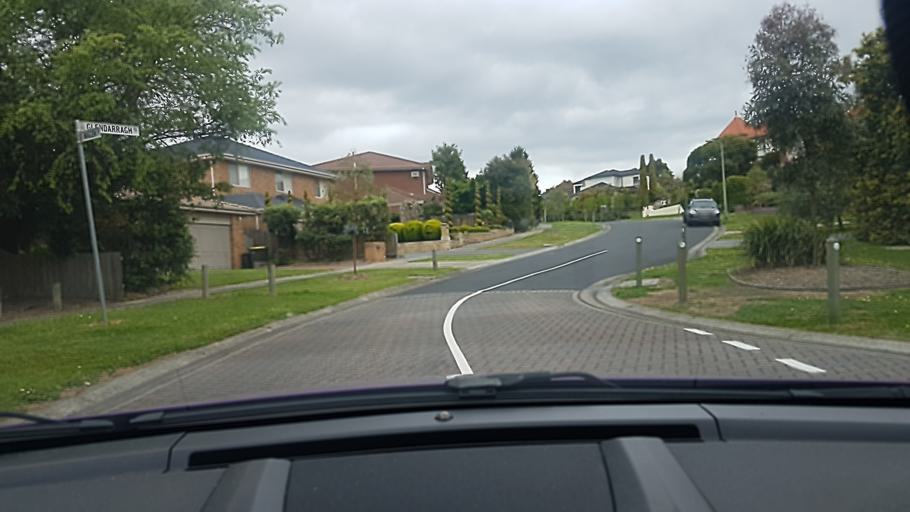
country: AU
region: Victoria
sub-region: Nillumbik
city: Eltham
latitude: -37.7606
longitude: 145.1623
